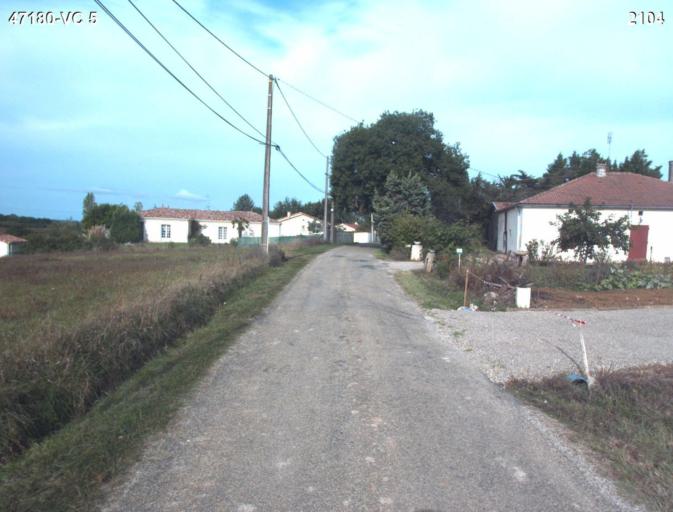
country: FR
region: Aquitaine
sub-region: Departement du Lot-et-Garonne
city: Sainte-Colombe-en-Bruilhois
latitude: 44.1659
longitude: 0.4719
